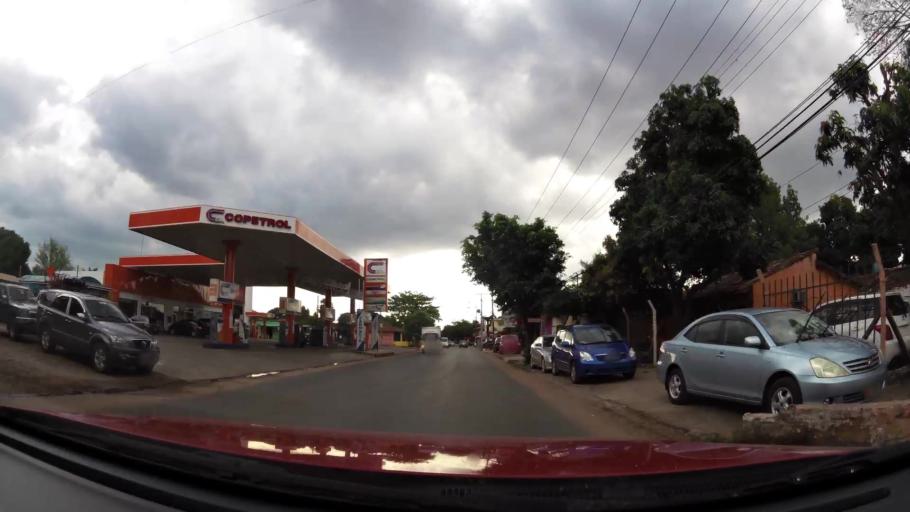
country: PY
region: Central
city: Fernando de la Mora
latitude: -25.3364
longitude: -57.5630
